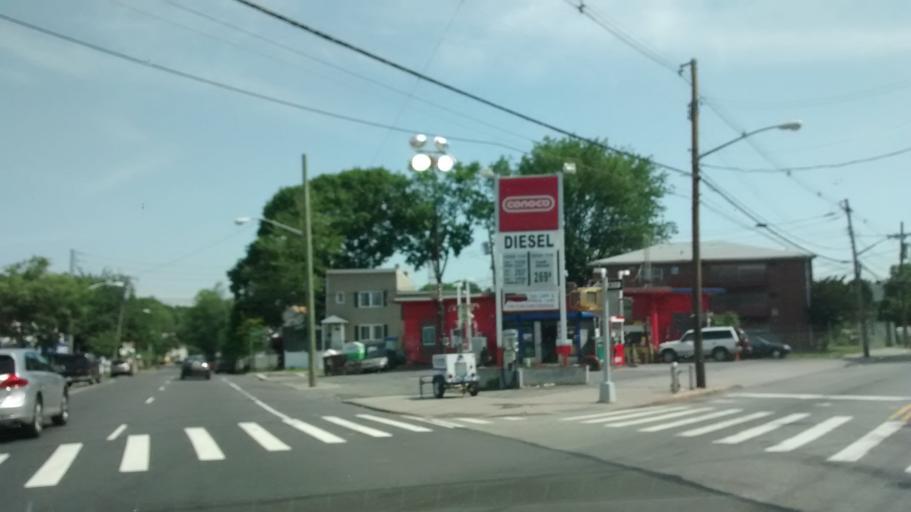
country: US
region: New Jersey
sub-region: Hudson County
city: Bayonne
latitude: 40.6152
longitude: -74.0847
